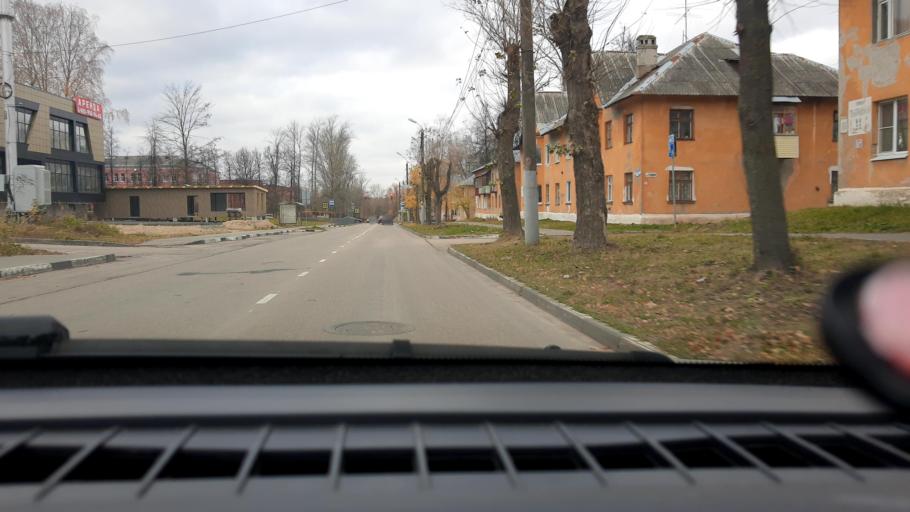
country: RU
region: Nizjnij Novgorod
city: Kstovo
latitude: 56.1518
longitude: 44.1976
